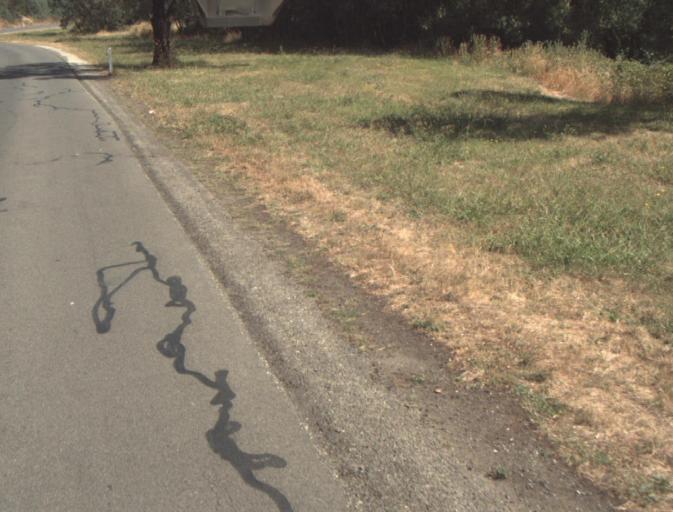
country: AU
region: Tasmania
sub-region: Launceston
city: Newstead
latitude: -41.4176
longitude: 147.1664
